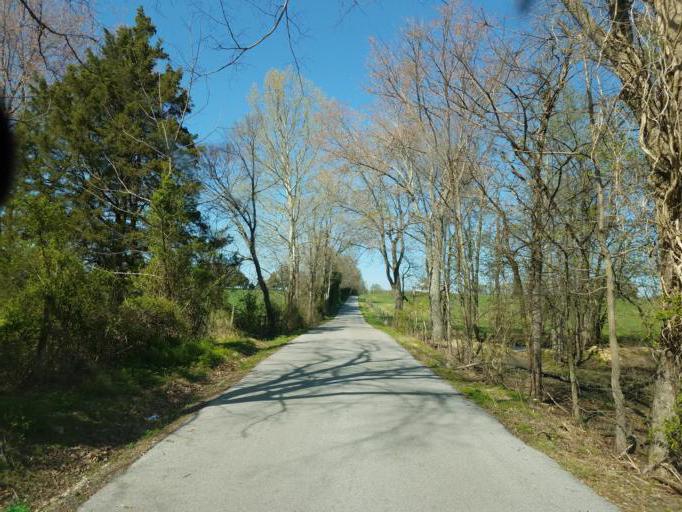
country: US
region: Kentucky
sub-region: Edmonson County
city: Brownsville
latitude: 37.1223
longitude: -86.1510
